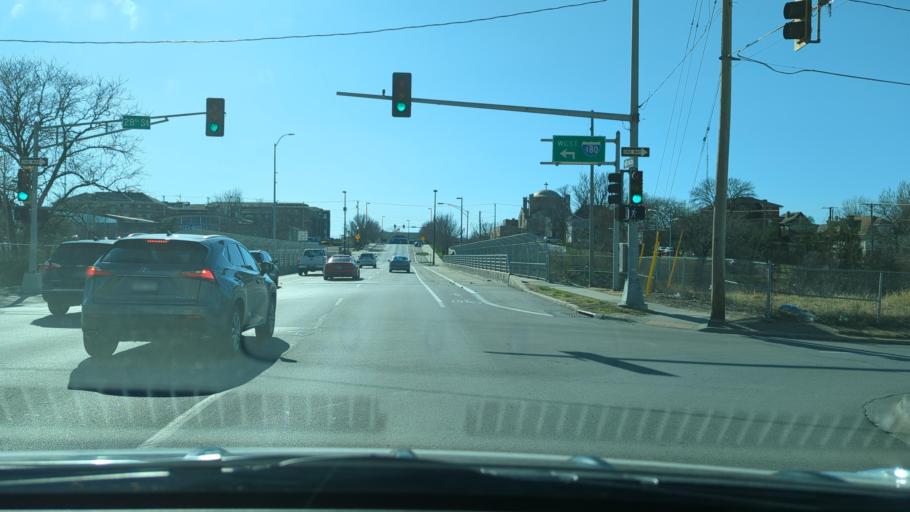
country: US
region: Nebraska
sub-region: Douglas County
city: Omaha
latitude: 41.2536
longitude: -95.9530
